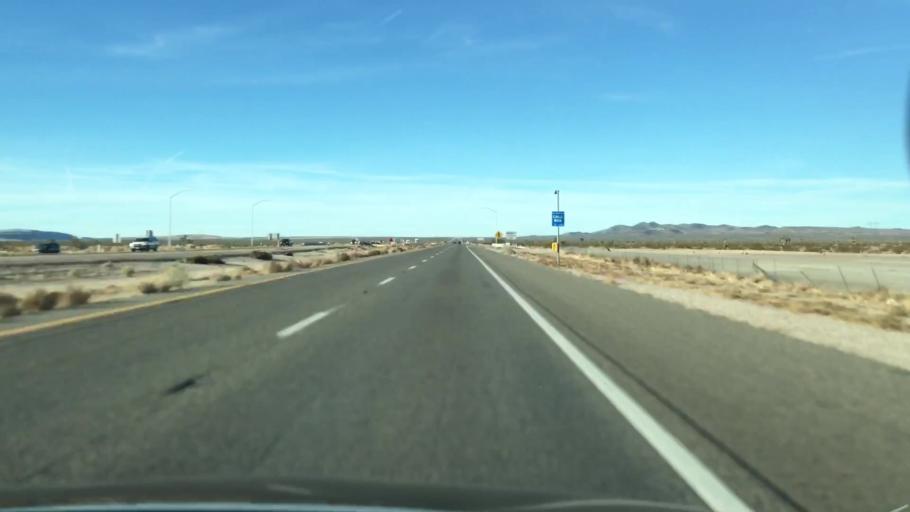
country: US
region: Nevada
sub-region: Clark County
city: Sandy Valley
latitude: 35.4347
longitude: -115.7013
